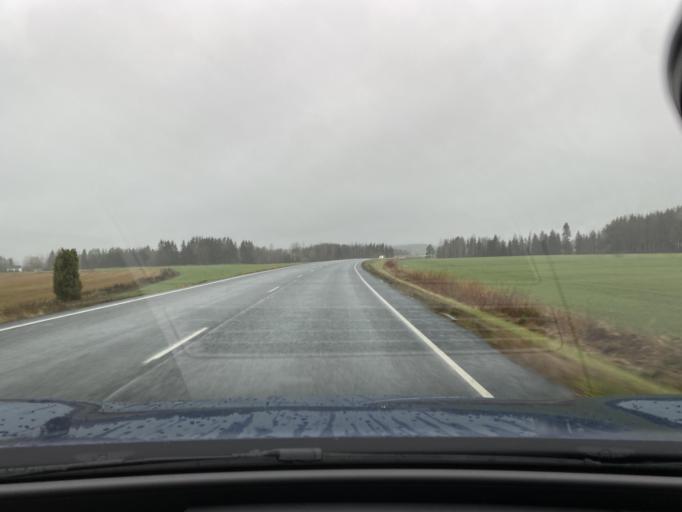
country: FI
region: Varsinais-Suomi
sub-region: Loimaa
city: Loimaa
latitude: 60.8814
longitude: 22.9820
